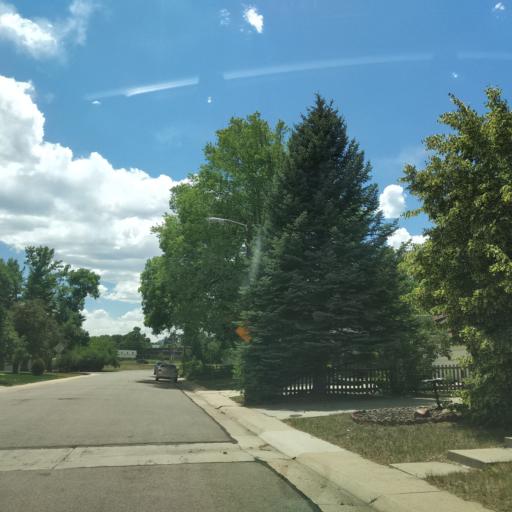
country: US
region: Colorado
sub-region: Jefferson County
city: Lakewood
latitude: 39.6838
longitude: -105.0945
